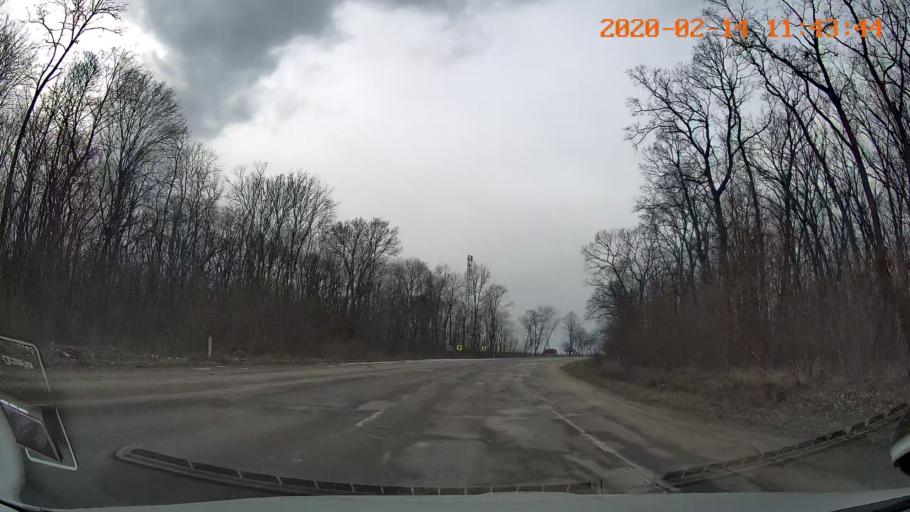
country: MD
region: Briceni
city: Briceni
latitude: 48.3312
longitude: 27.0478
